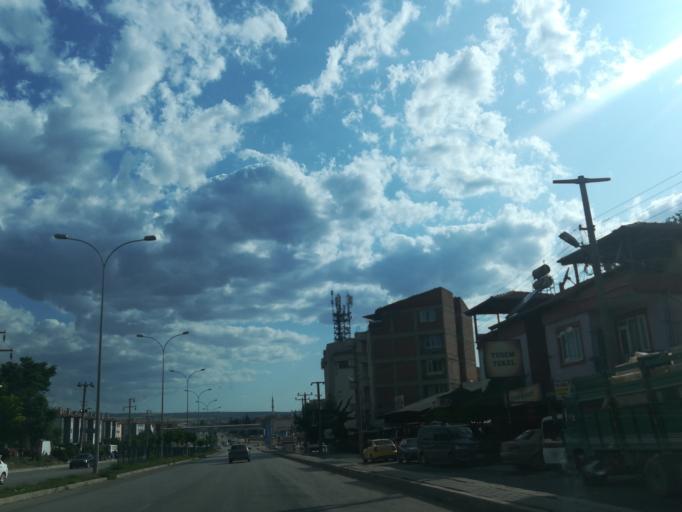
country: TR
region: Afyonkarahisar
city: Dinar
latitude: 38.0668
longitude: 30.1676
